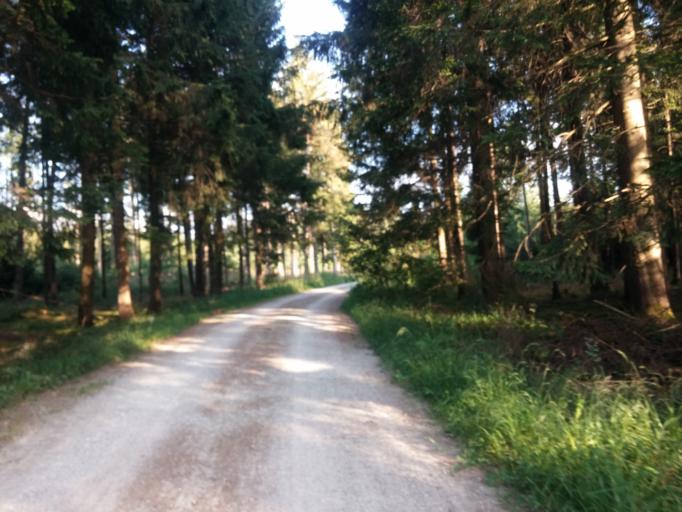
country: DE
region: Bavaria
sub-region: Upper Bavaria
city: Grasbrunn
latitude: 48.0680
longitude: 11.7591
